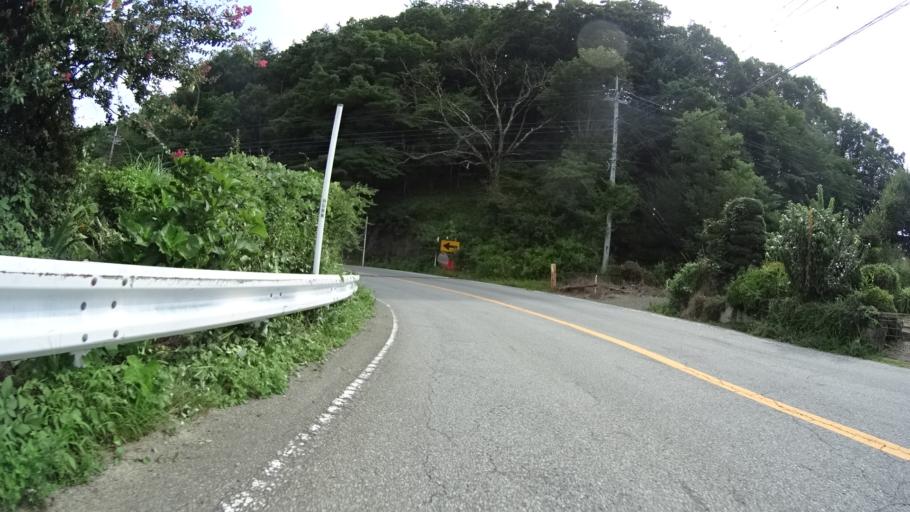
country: JP
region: Yamanashi
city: Kofu-shi
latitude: 35.7025
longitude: 138.5586
